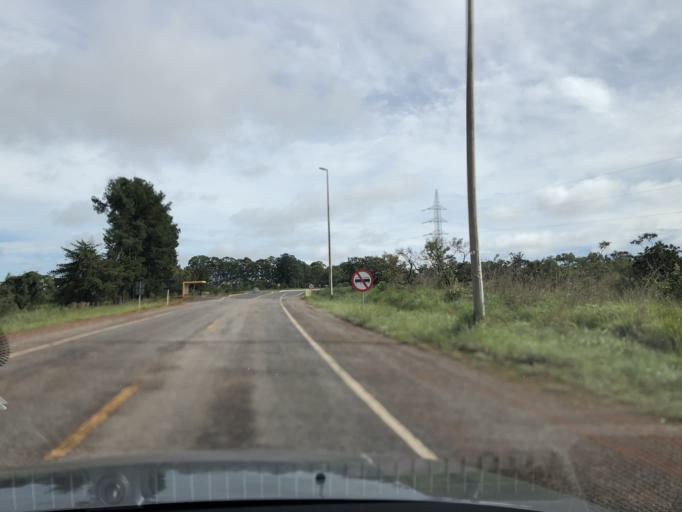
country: BR
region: Federal District
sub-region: Brasilia
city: Brasilia
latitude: -15.6795
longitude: -48.0898
